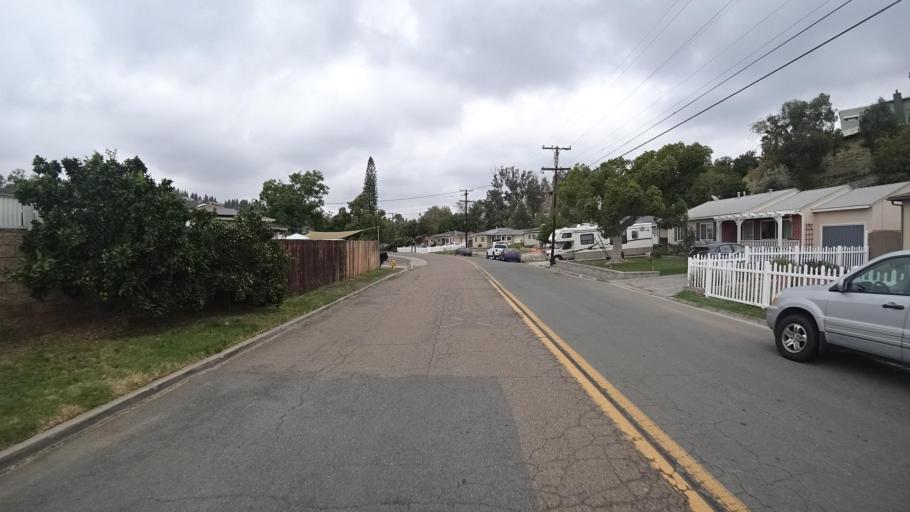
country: US
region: California
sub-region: San Diego County
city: Spring Valley
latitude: 32.7488
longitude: -117.0123
